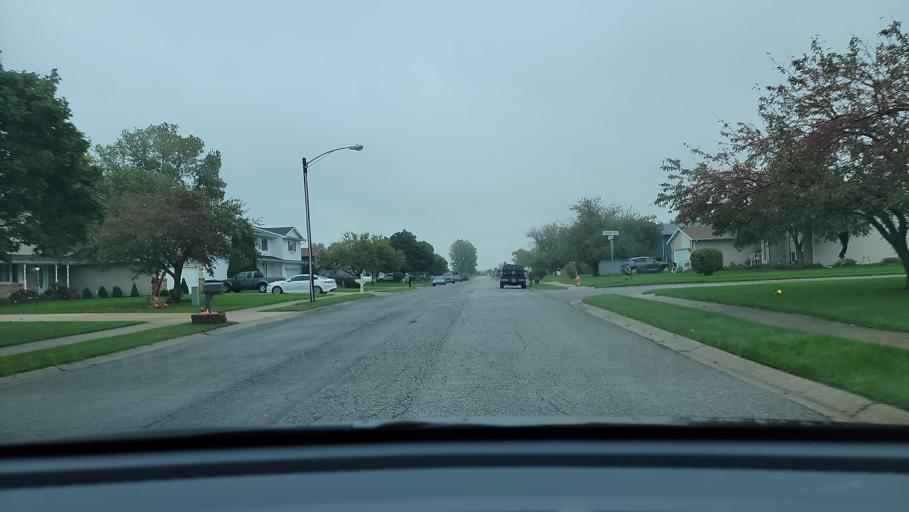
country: US
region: Indiana
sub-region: Porter County
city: Portage
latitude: 41.5438
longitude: -87.1962
